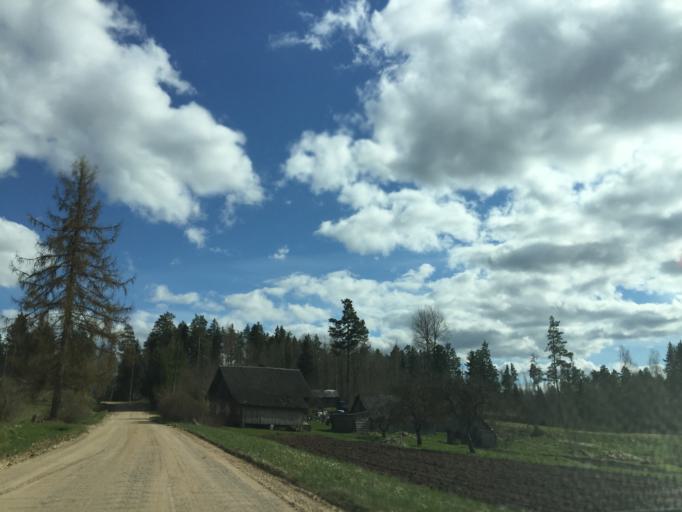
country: LV
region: Rezekne
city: Rezekne
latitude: 56.6577
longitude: 27.2725
